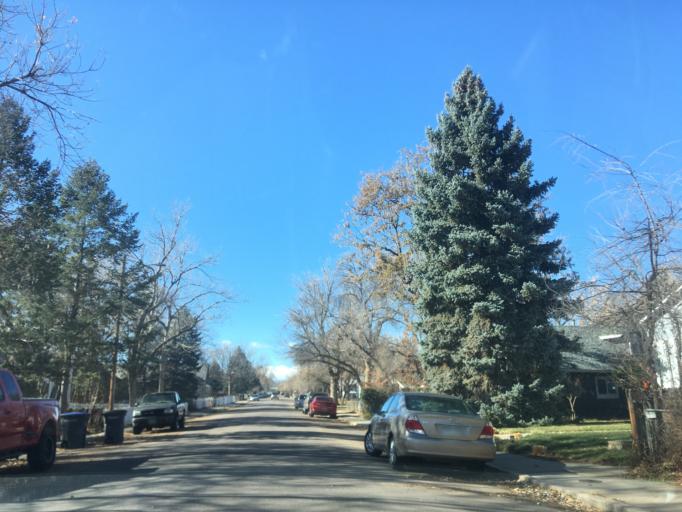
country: US
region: Colorado
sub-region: Boulder County
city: Lafayette
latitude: 39.9942
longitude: -105.0827
